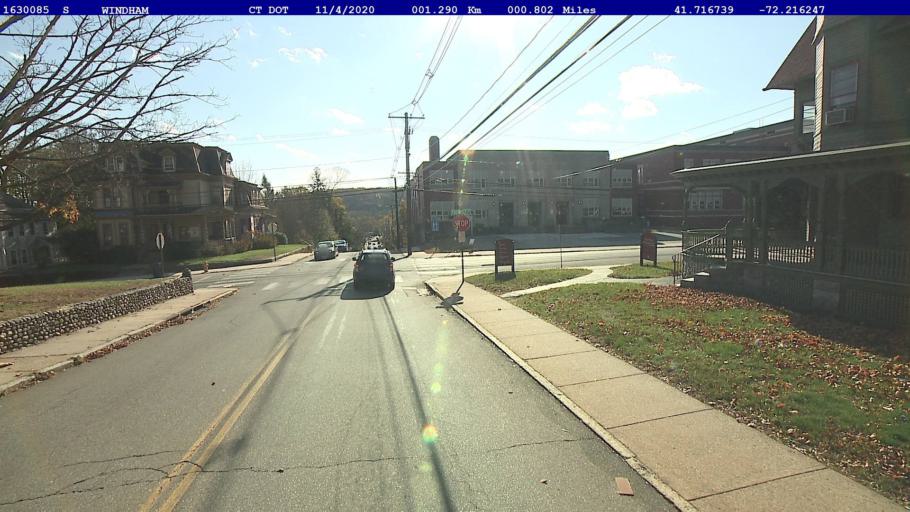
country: US
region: Connecticut
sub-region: Windham County
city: Willimantic
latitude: 41.7167
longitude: -72.2162
